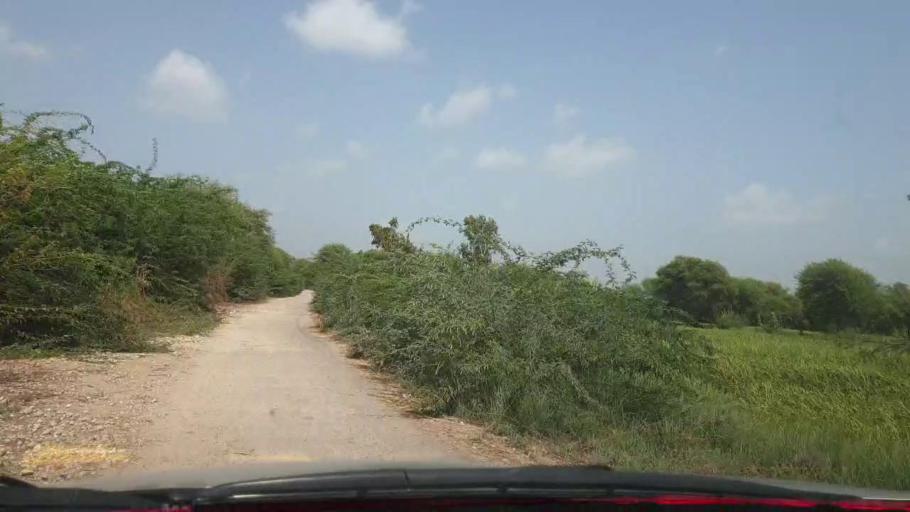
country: PK
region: Sindh
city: Tando Bago
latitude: 24.8644
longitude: 68.9226
